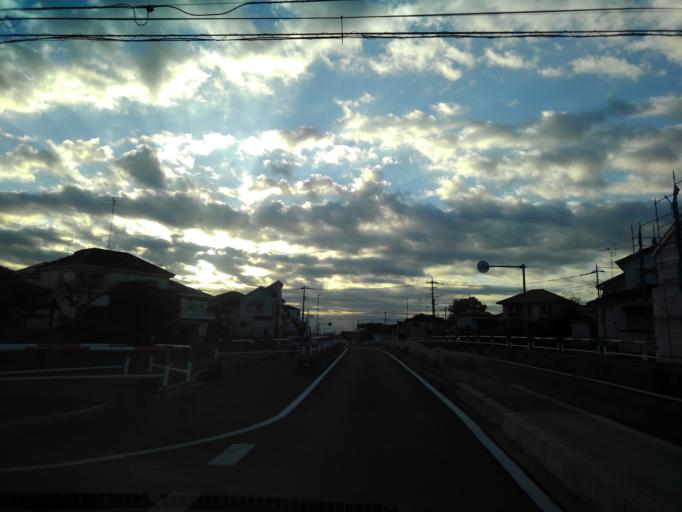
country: JP
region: Saitama
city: Tokorozawa
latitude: 35.7832
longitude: 139.4544
